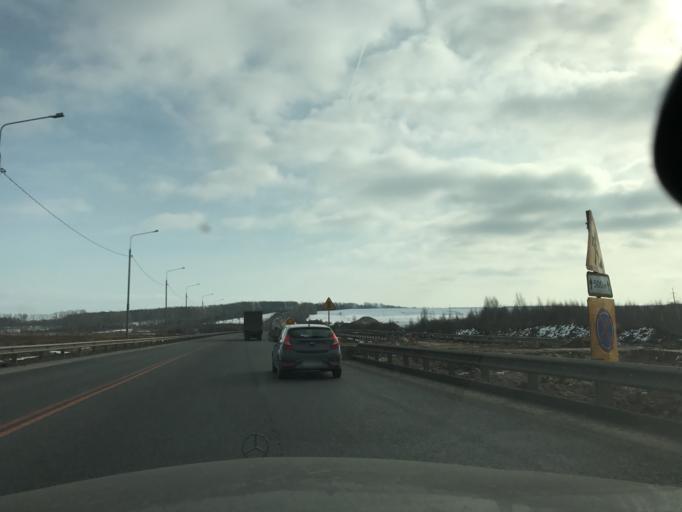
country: RU
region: Vladimir
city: Novovyazniki
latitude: 56.2172
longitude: 42.2291
